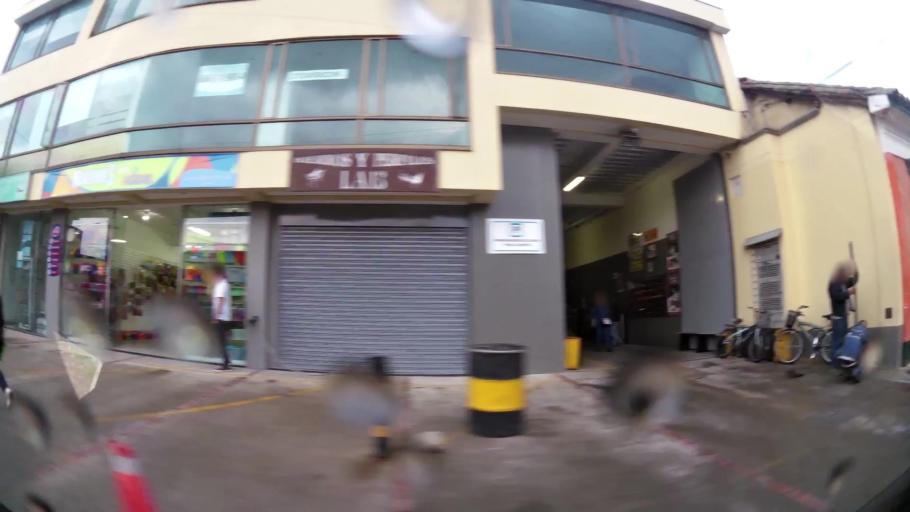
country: CO
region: Cundinamarca
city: Chia
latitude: 4.8635
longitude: -74.0597
